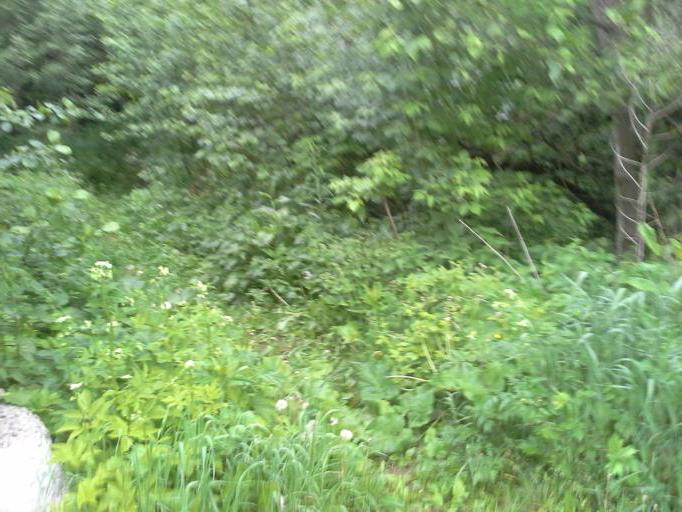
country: RU
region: Moskovskaya
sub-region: Leninskiy Rayon
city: Vnukovo
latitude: 55.6264
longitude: 37.2727
